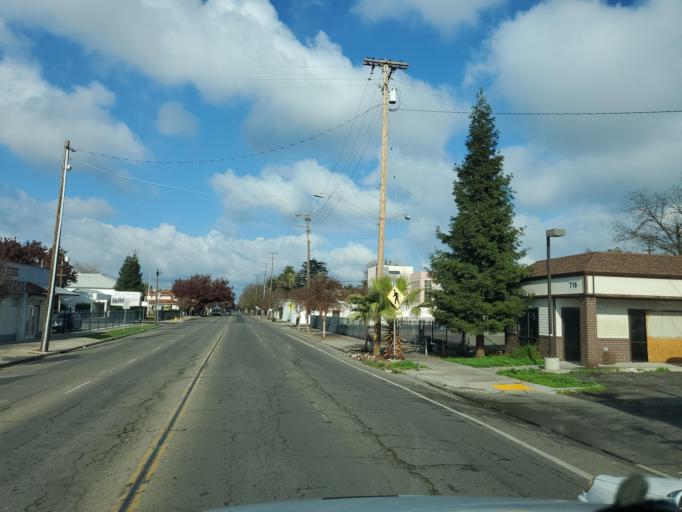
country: US
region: California
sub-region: San Joaquin County
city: Stockton
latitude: 37.9608
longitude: -121.2865
